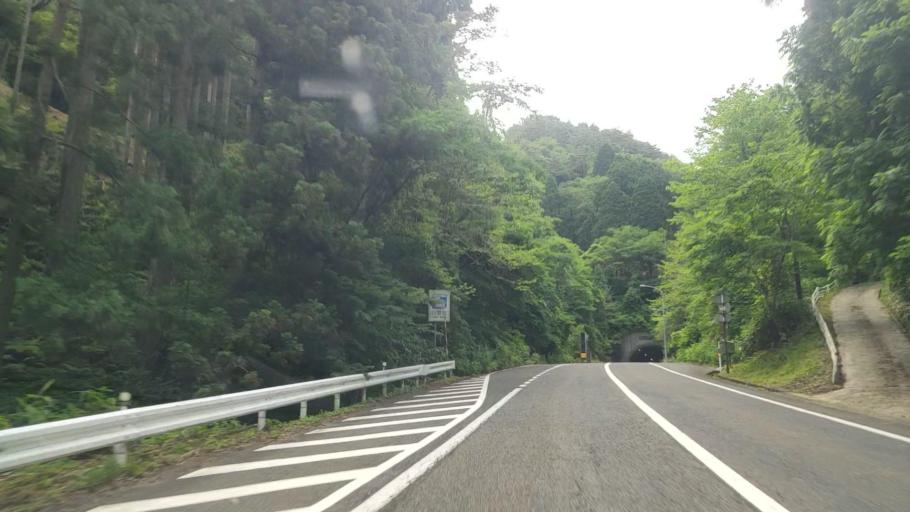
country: JP
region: Tottori
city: Yonago
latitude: 35.2707
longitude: 133.4343
